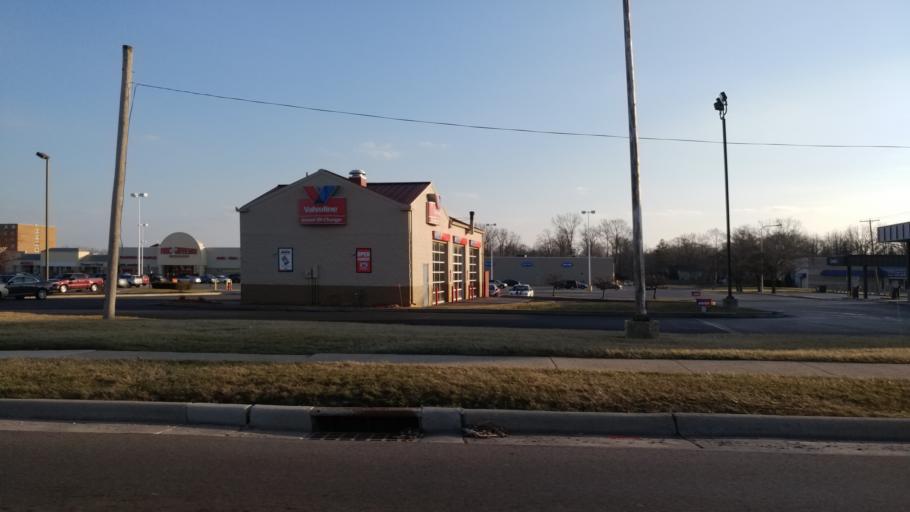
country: US
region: Ohio
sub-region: Hancock County
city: Findlay
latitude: 41.0534
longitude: -83.6112
